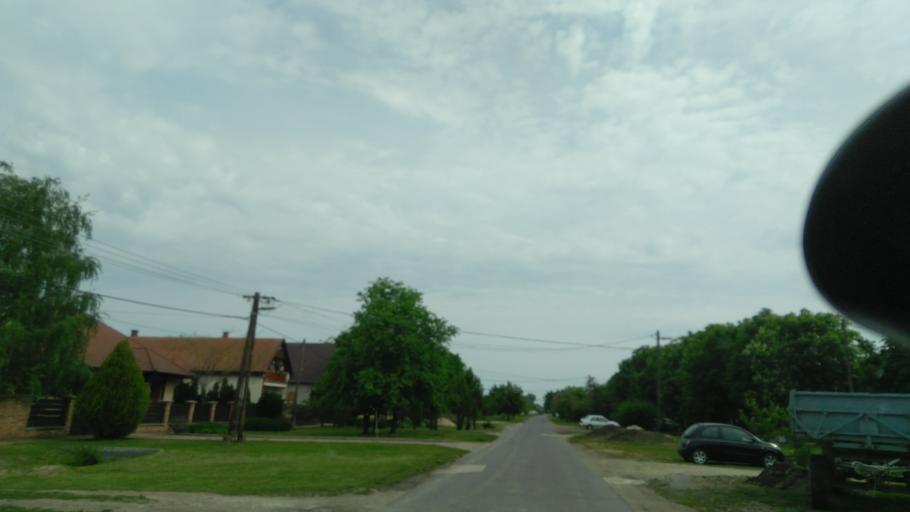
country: HU
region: Bekes
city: Szeghalom
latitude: 47.0185
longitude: 21.1673
